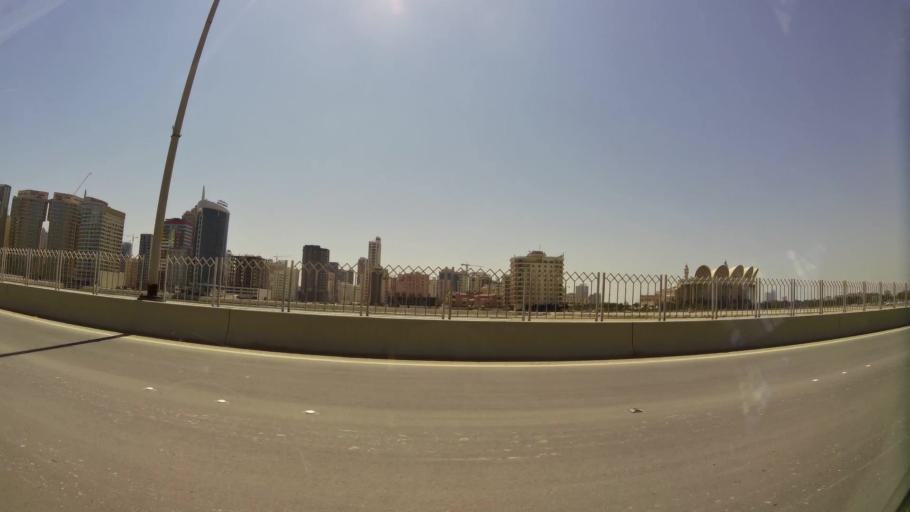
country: BH
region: Manama
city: Manama
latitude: 26.2236
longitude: 50.6024
